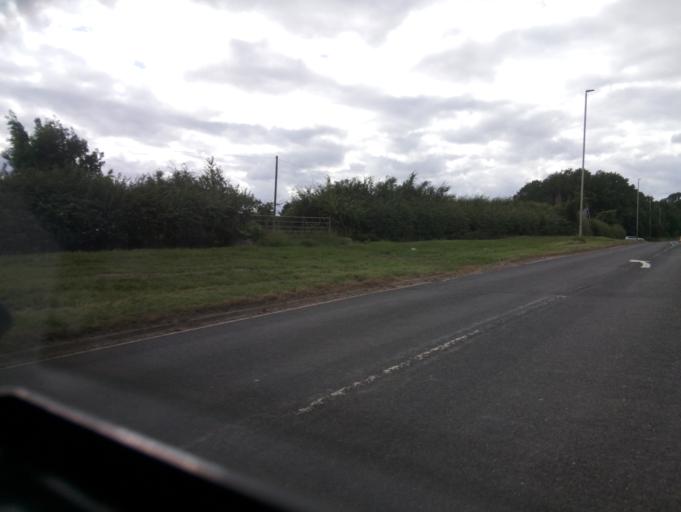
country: GB
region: England
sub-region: Warwickshire
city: Atherstone
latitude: 52.6269
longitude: -1.4848
